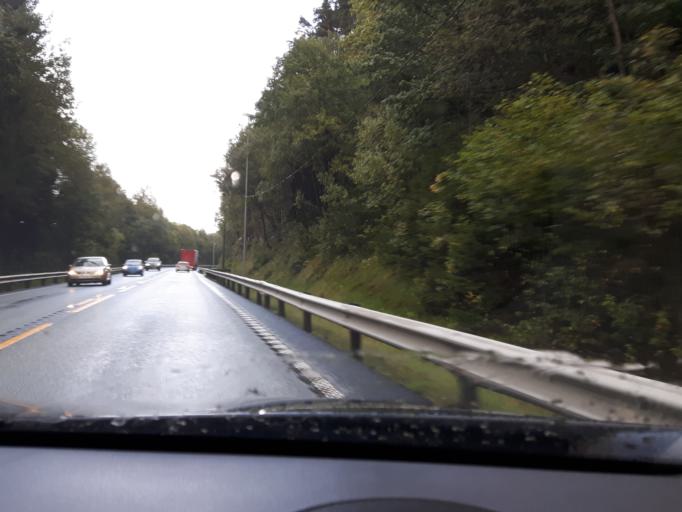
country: NO
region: Vest-Agder
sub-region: Sogne
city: Sogne
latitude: 58.0940
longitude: 7.7526
